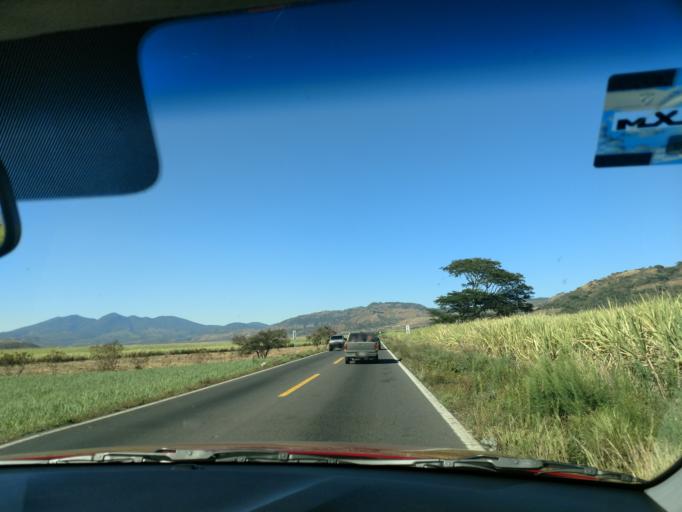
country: MX
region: Nayarit
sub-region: Ahuacatlan
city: Ahuacatlan
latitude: 21.1394
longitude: -104.6076
